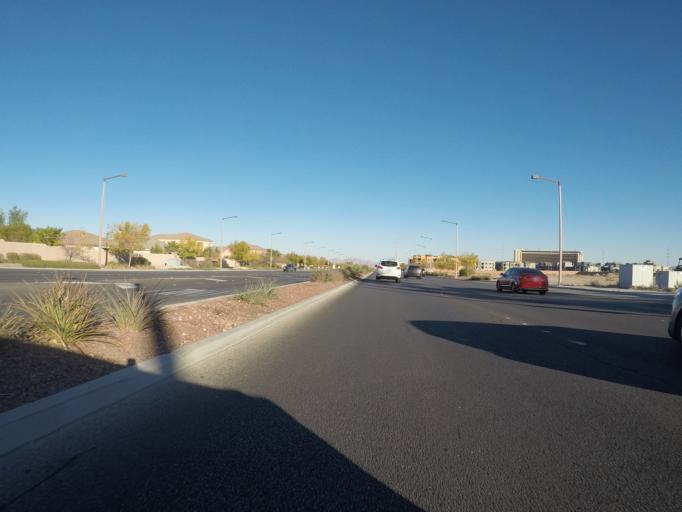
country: US
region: Nevada
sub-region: Clark County
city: Summerlin South
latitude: 36.1589
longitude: -115.3440
